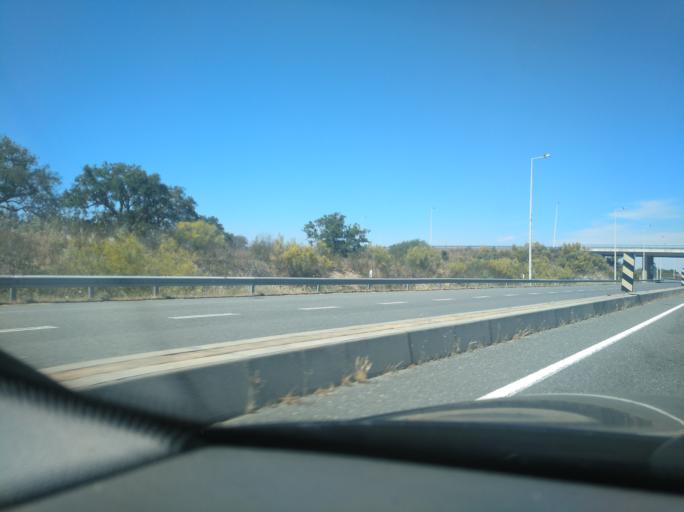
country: PT
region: Beja
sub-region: Ourique
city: Ourique
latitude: 37.6702
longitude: -8.1554
